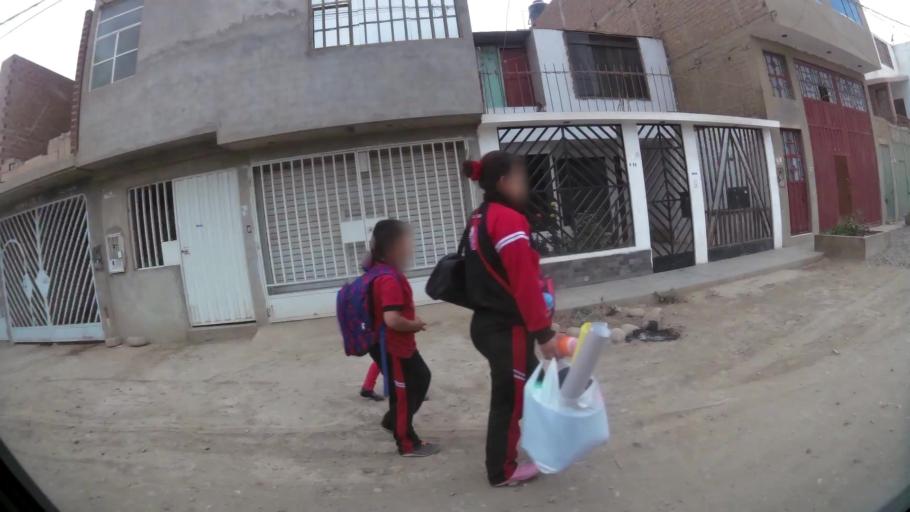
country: PE
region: Lima
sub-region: Lima
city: Independencia
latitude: -11.9612
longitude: -77.0984
